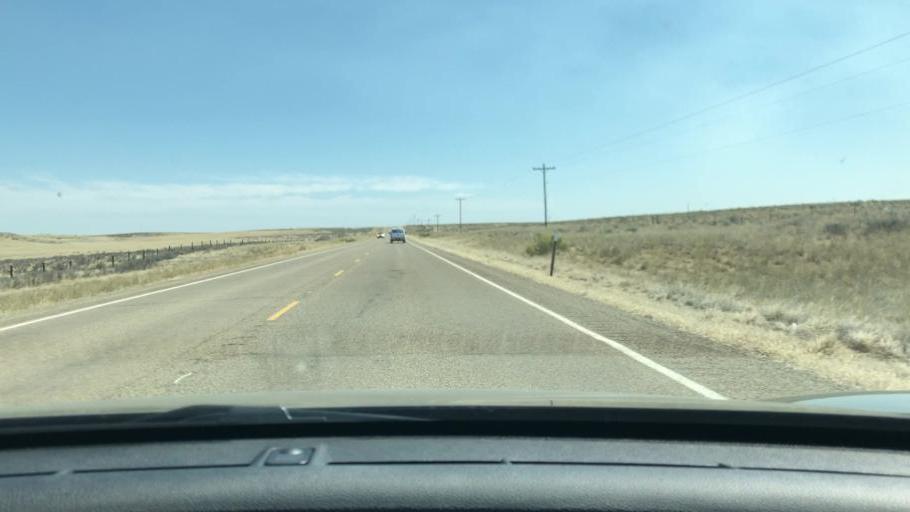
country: US
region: Idaho
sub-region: Owyhee County
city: Homedale
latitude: 42.8553
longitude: -117.5802
